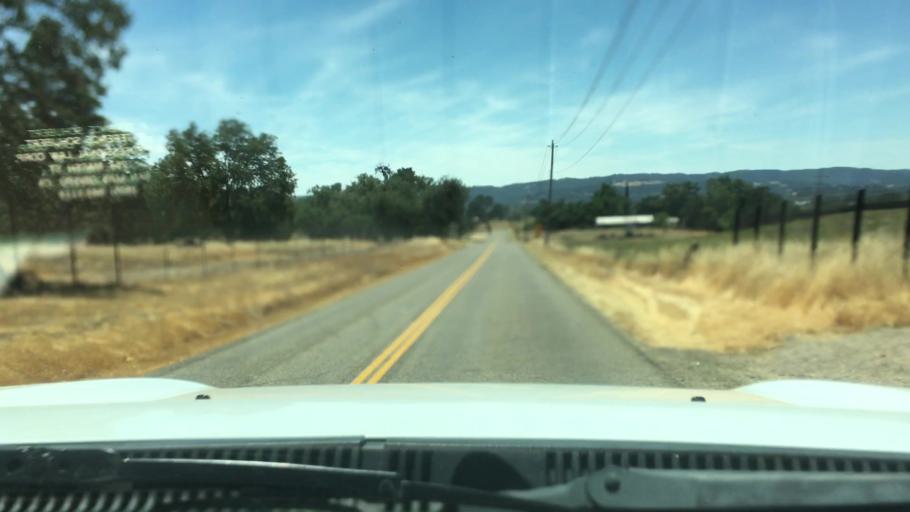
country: US
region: California
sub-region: San Luis Obispo County
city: Templeton
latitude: 35.5703
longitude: -120.6635
